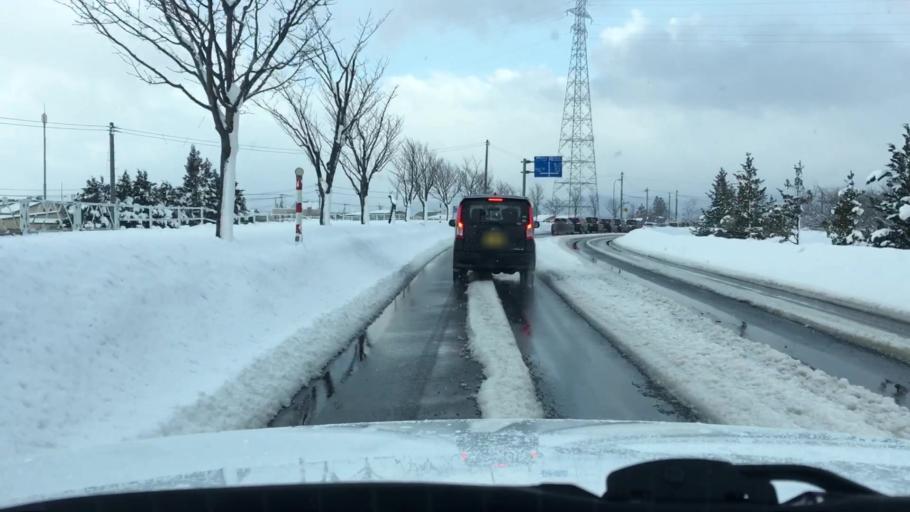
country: JP
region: Aomori
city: Hirosaki
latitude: 40.6294
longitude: 140.4742
